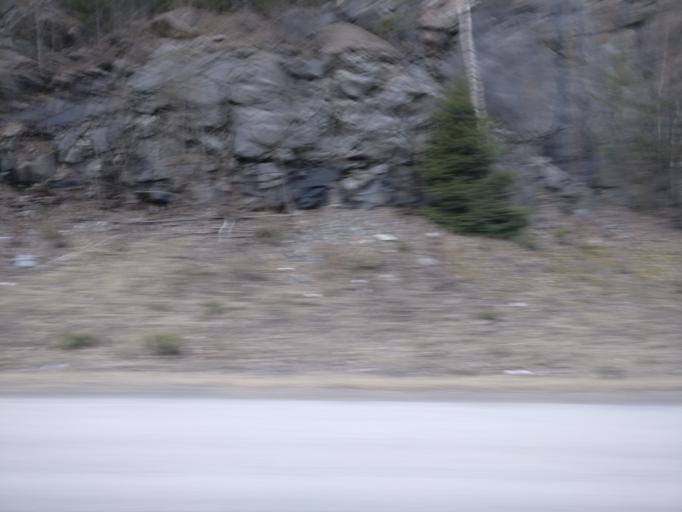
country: FI
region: Uusimaa
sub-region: Helsinki
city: Nurmijaervi
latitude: 60.3873
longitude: 24.8145
